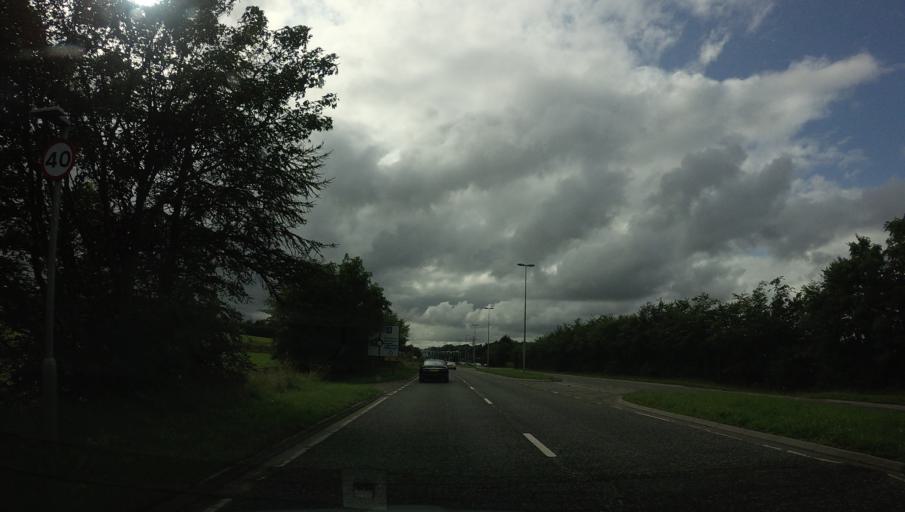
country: GB
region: Scotland
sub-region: Aberdeen City
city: Cults
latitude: 57.1462
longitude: -2.2153
